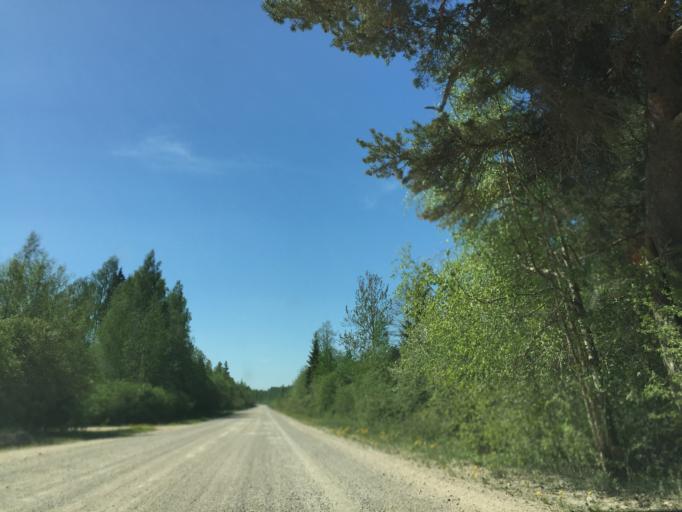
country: LV
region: Kegums
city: Kegums
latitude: 56.8828
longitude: 24.7860
